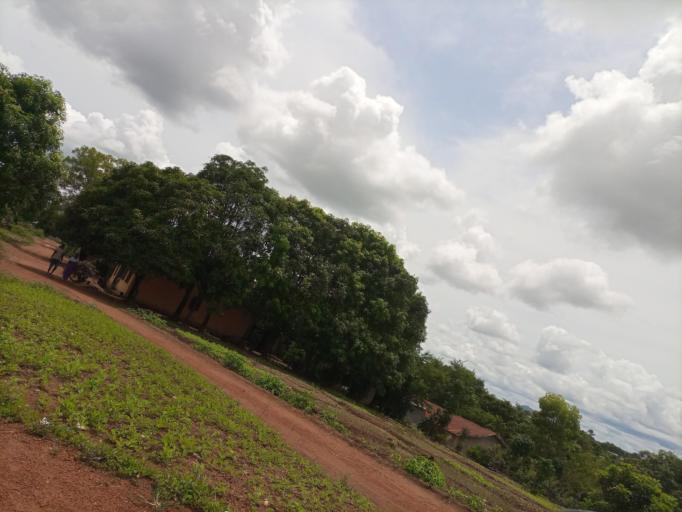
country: SL
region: Southern Province
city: Baoma
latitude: 7.9720
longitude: -11.7141
